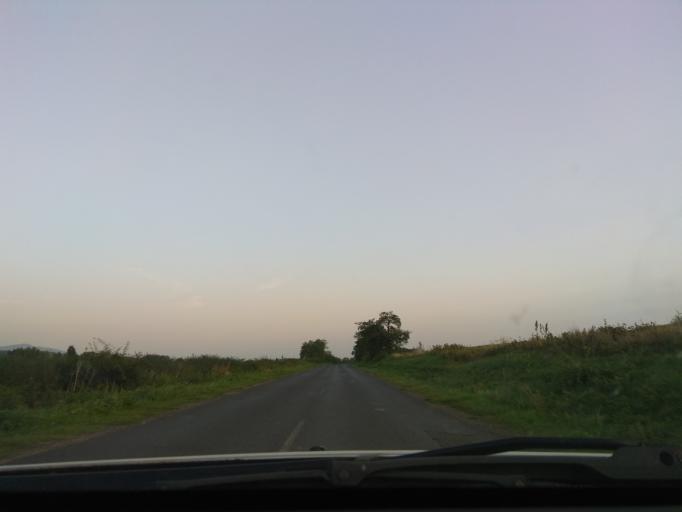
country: HU
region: Borsod-Abauj-Zemplen
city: Tallya
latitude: 48.2014
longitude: 21.2125
